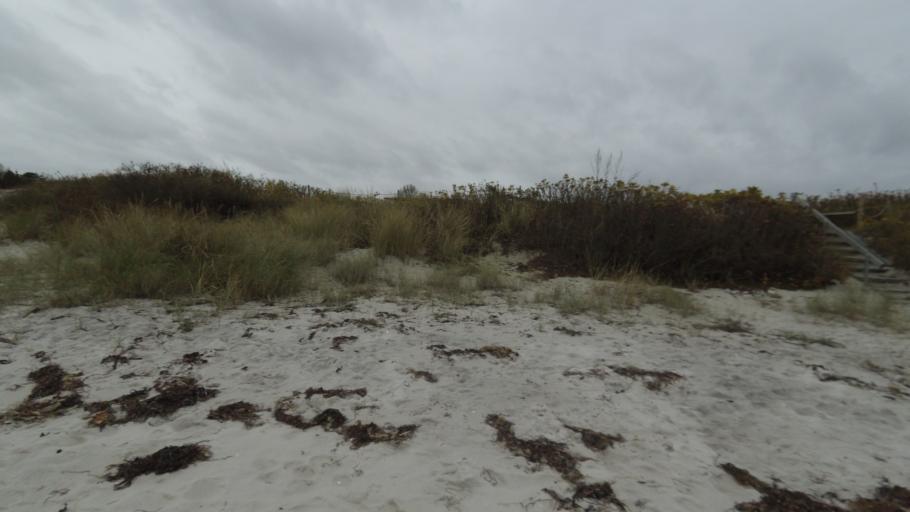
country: DK
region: Central Jutland
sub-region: Arhus Kommune
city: Malling
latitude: 55.9728
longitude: 10.2557
